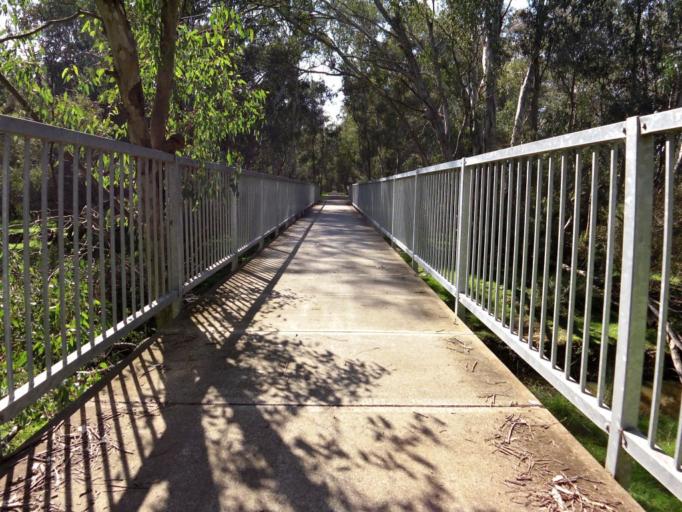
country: AU
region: Victoria
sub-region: Murrindindi
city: Alexandra
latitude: -37.1596
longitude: 145.5657
